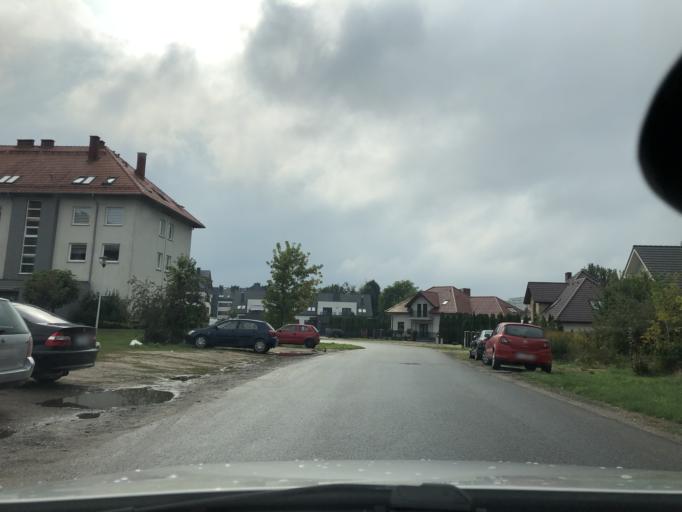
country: PL
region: Greater Poland Voivodeship
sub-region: Powiat pilski
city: Pila
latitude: 53.1566
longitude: 16.7619
